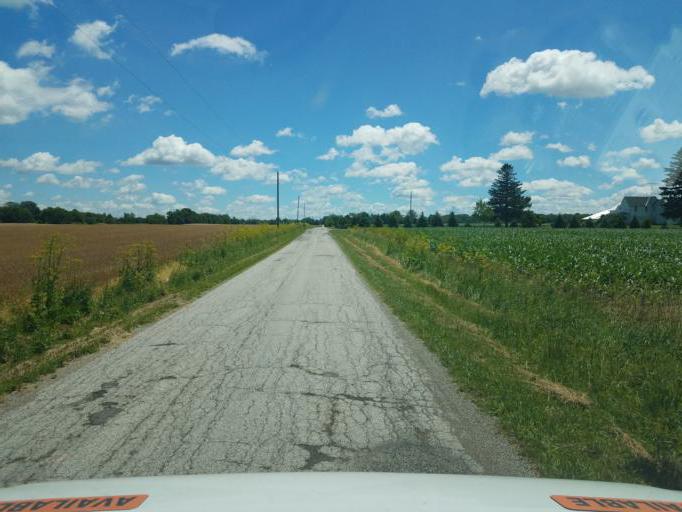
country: US
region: Ohio
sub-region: Crawford County
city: Galion
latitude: 40.7125
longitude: -82.8553
